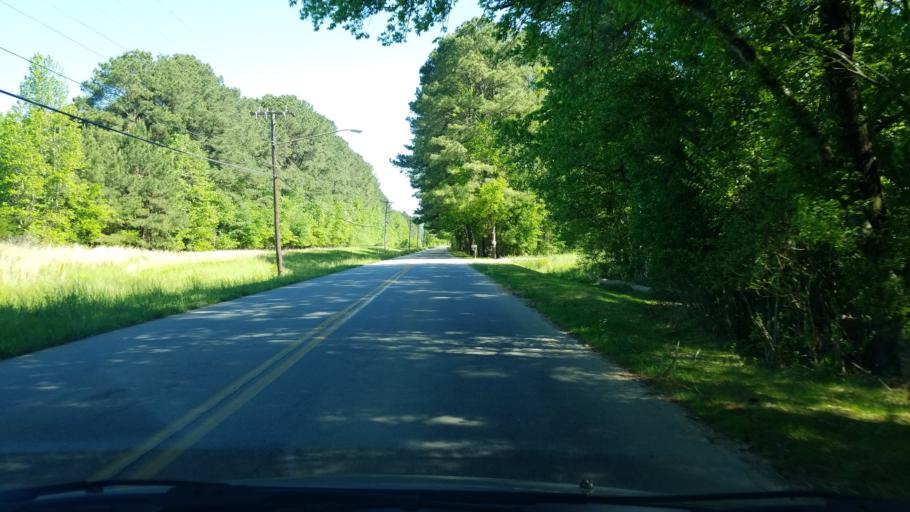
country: US
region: Tennessee
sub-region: Hamilton County
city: Chattanooga
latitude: 35.0363
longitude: -85.3346
